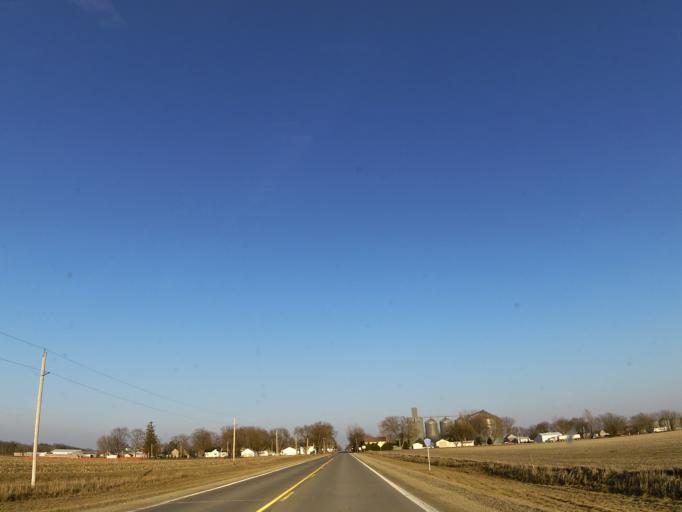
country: US
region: Iowa
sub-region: Mitchell County
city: Saint Ansgar
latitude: 43.4150
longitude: -93.0235
